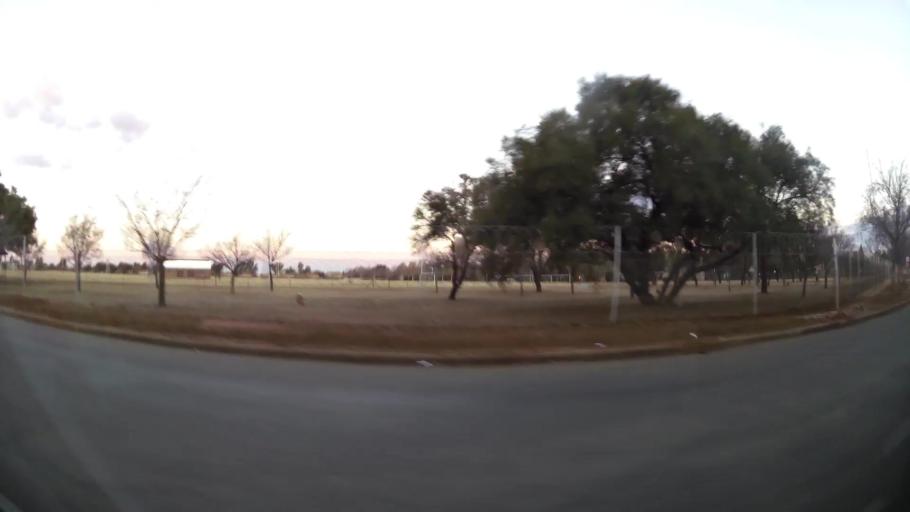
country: ZA
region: North-West
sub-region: Dr Kenneth Kaunda District Municipality
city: Potchefstroom
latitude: -26.7094
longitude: 27.1164
